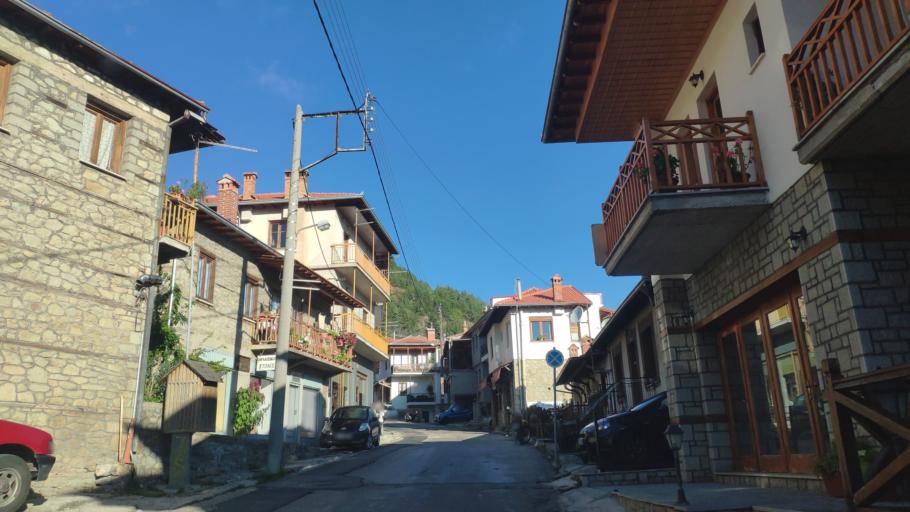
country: GR
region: Epirus
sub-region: Nomos Ioanninon
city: Metsovo
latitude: 39.7724
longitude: 21.1810
